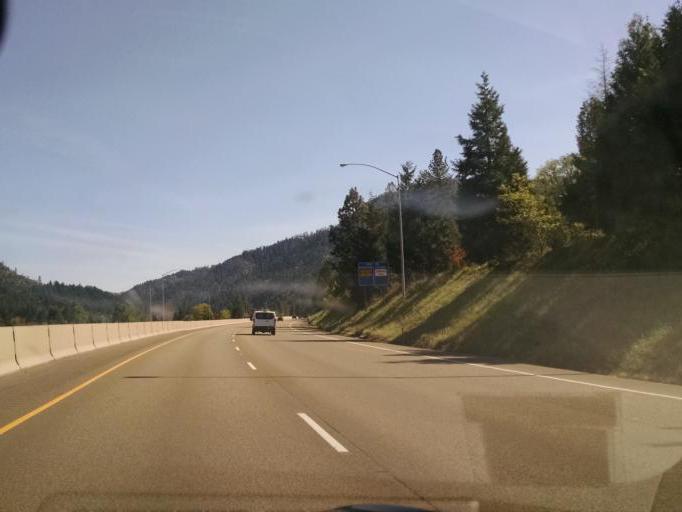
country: US
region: Oregon
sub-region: Douglas County
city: Canyonville
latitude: 42.9380
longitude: -123.2856
